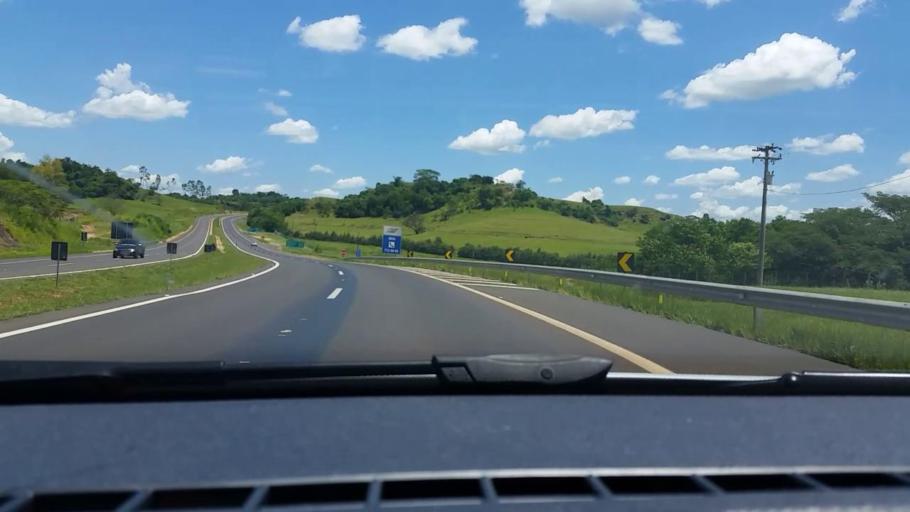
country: BR
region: Sao Paulo
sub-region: Bauru
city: Bauru
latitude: -22.4282
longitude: -49.1315
